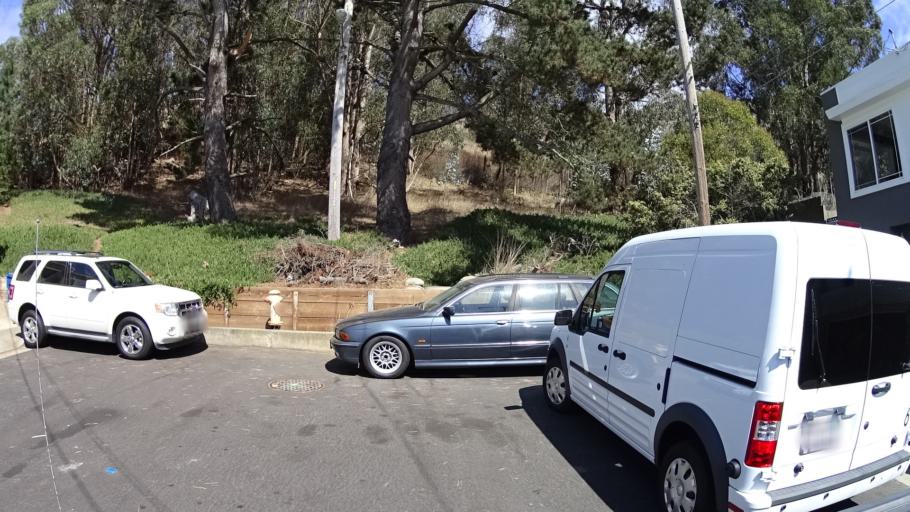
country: US
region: California
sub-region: San Mateo County
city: Daly City
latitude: 37.6920
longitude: -122.4541
